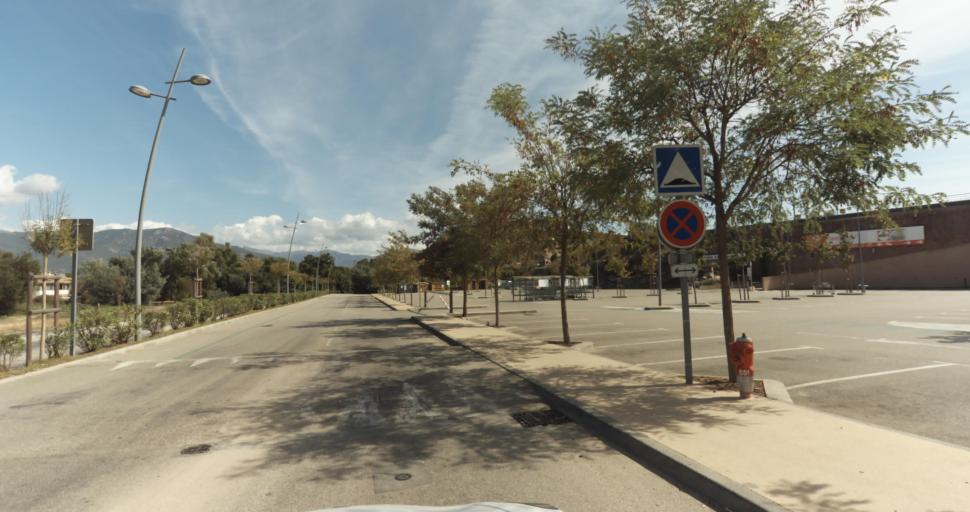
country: FR
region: Corsica
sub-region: Departement de la Corse-du-Sud
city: Afa
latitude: 41.9512
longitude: 8.7754
